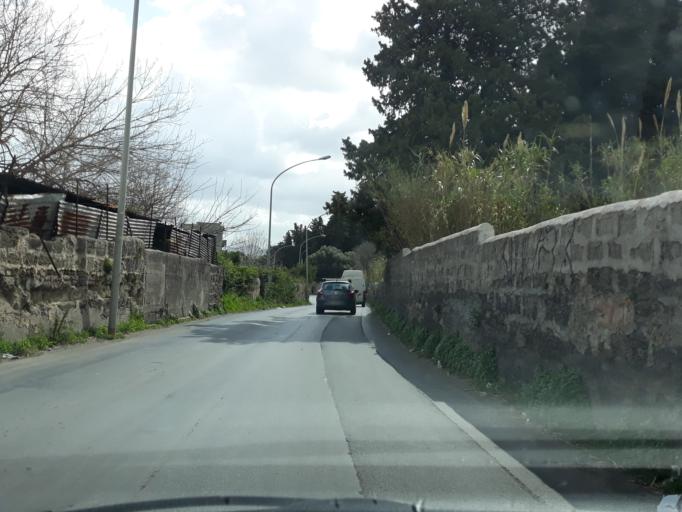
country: IT
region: Sicily
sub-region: Palermo
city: Palermo
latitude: 38.1257
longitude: 13.3145
